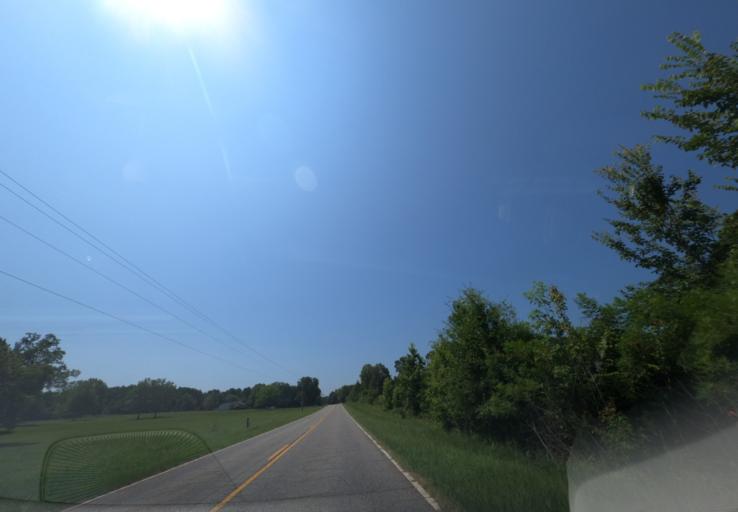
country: US
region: South Carolina
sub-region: Greenwood County
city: Greenwood
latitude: 34.0527
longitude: -82.1366
